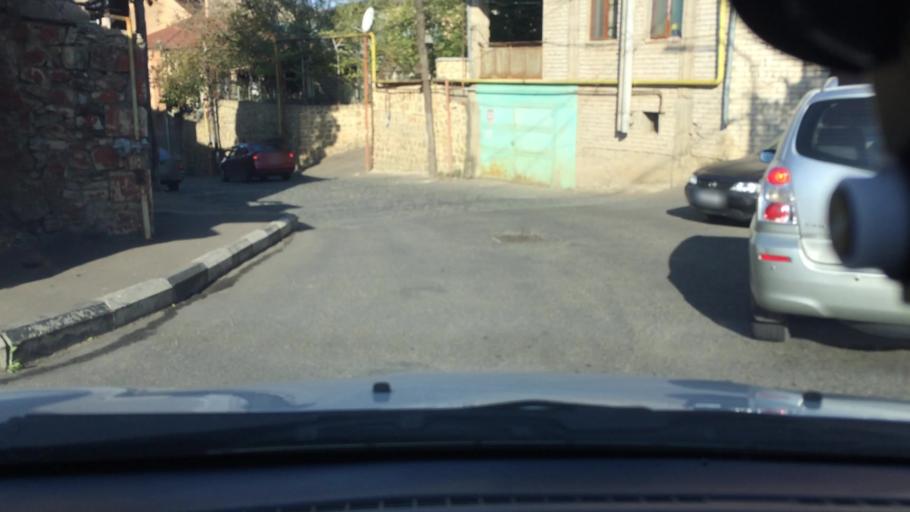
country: GE
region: Imereti
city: Kutaisi
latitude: 42.2725
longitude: 42.7116
